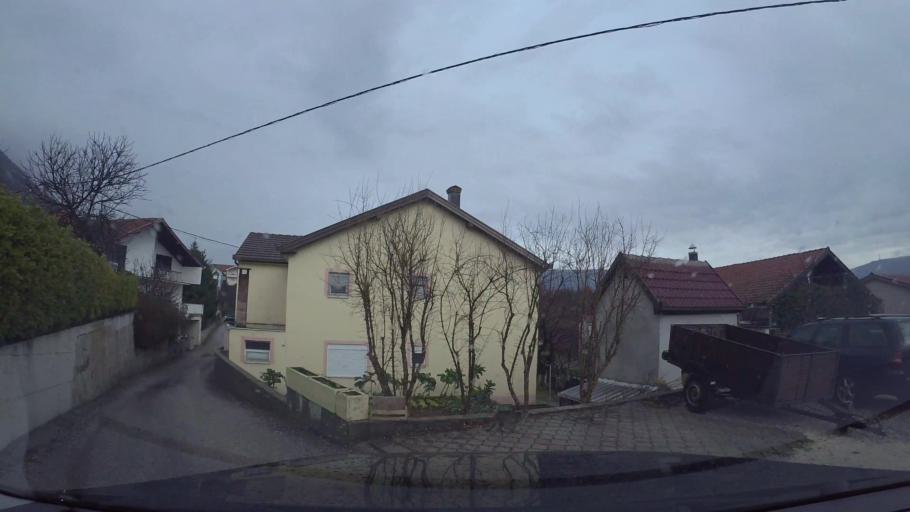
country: BA
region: Federation of Bosnia and Herzegovina
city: Cim
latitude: 43.3508
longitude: 17.7785
